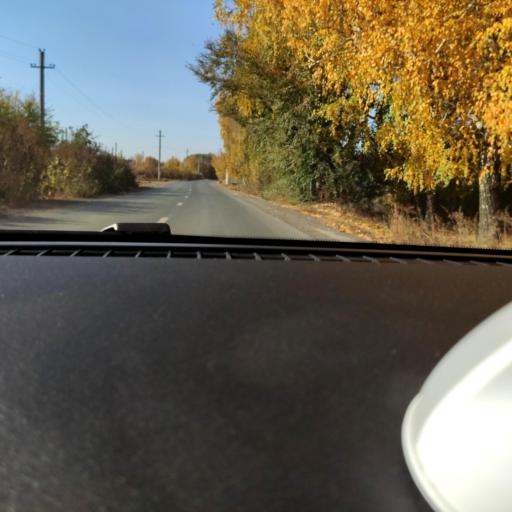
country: RU
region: Samara
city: Smyshlyayevka
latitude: 53.2431
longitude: 50.3569
